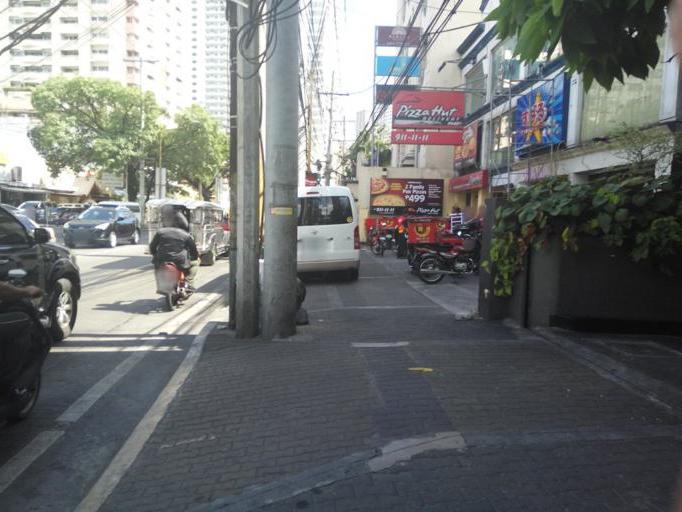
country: PH
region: Metro Manila
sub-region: Makati City
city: Makati City
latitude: 14.5540
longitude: 121.0138
